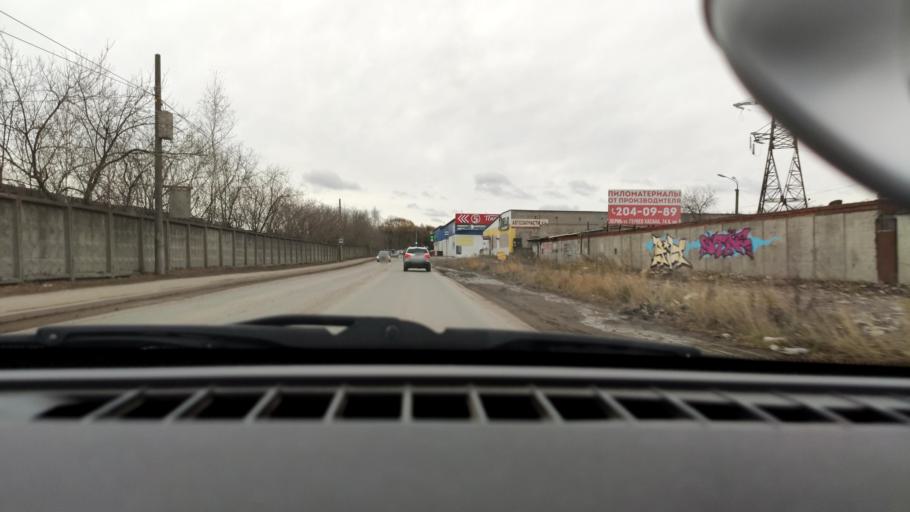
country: RU
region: Perm
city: Froly
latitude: 57.9518
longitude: 56.2609
